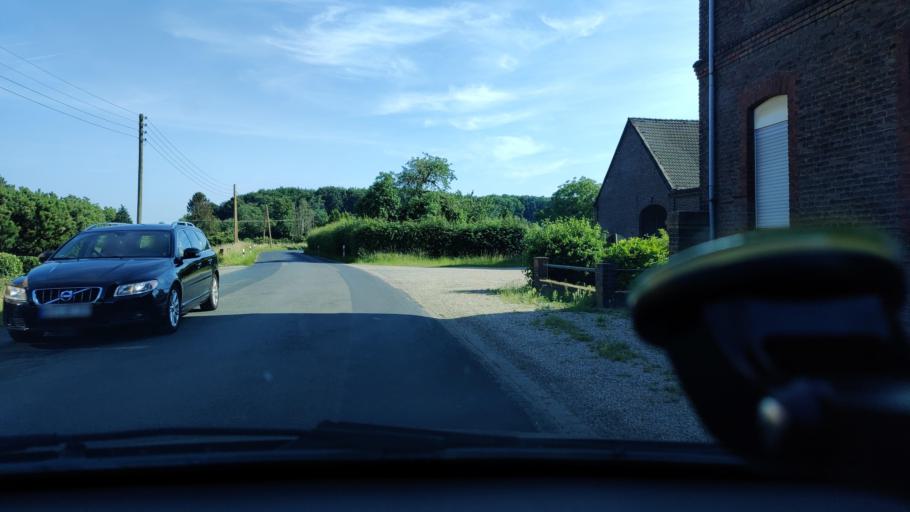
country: DE
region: North Rhine-Westphalia
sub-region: Regierungsbezirk Dusseldorf
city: Kamp-Lintfort
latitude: 51.5189
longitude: 6.5154
